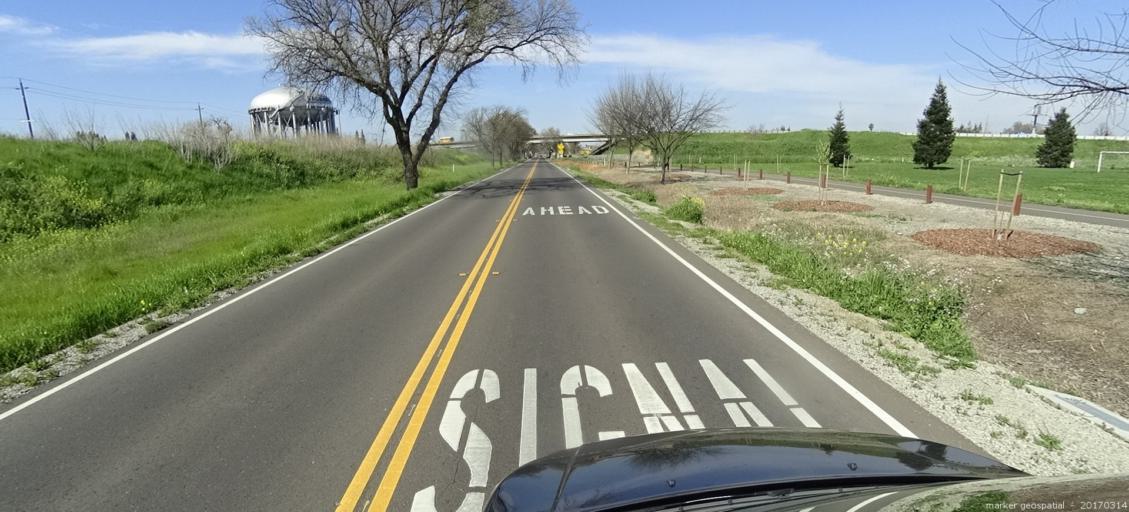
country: US
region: California
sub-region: Sacramento County
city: Parkway
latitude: 38.4727
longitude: -121.5040
